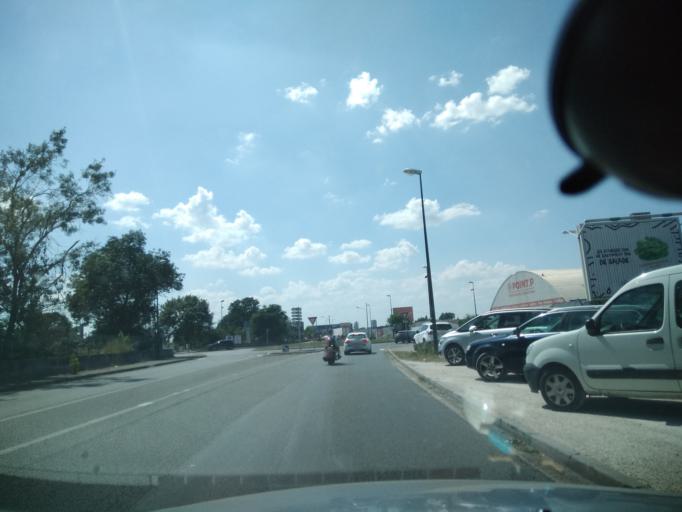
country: FR
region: Centre
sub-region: Departement d'Indre-et-Loire
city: Saint-Avertin
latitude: 47.3802
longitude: 0.7276
